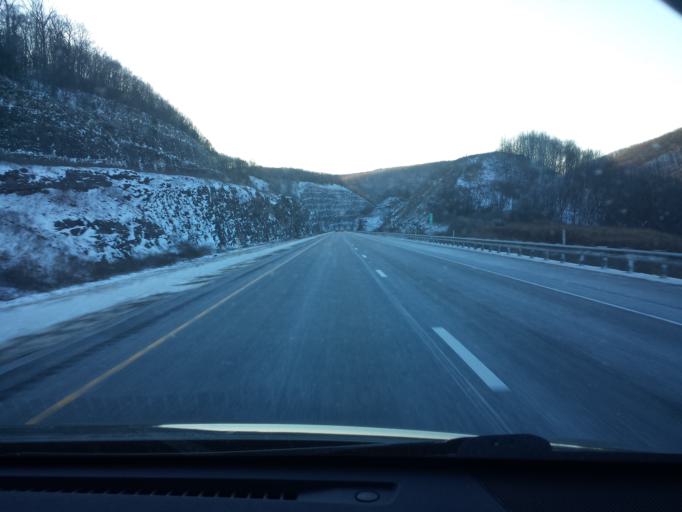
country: US
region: Pennsylvania
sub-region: Clinton County
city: Castanea
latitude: 41.0616
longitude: -77.3782
